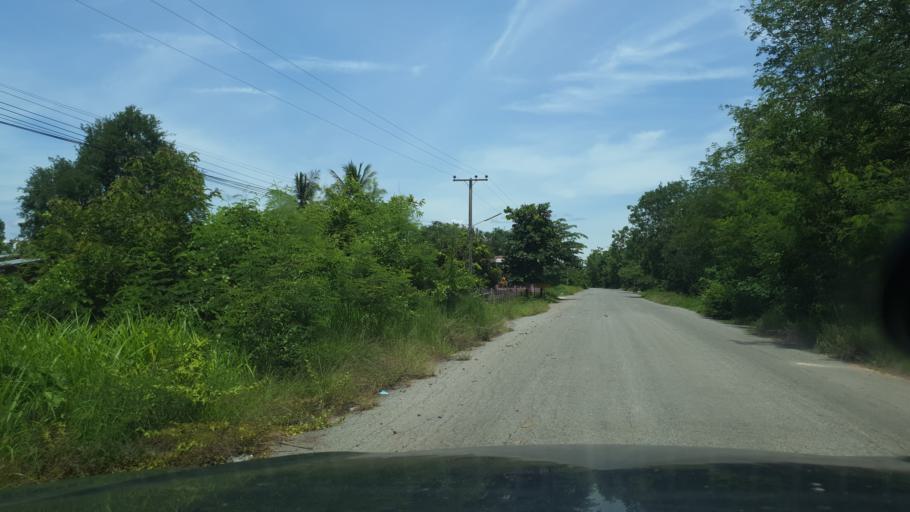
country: TH
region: Sukhothai
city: Ban Na
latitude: 17.0938
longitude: 99.6814
